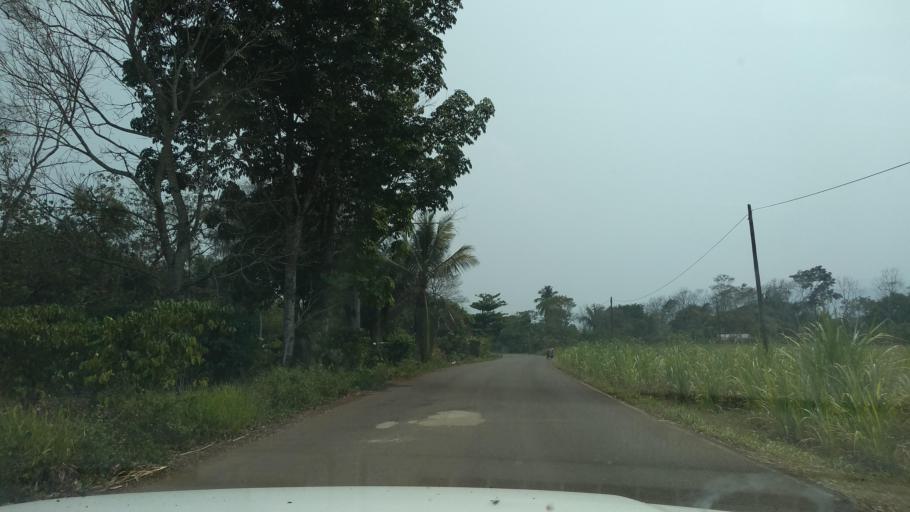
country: MX
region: Veracruz
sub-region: Tezonapa
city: Laguna Chica (Pueblo Nuevo)
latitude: 18.5297
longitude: -96.7695
